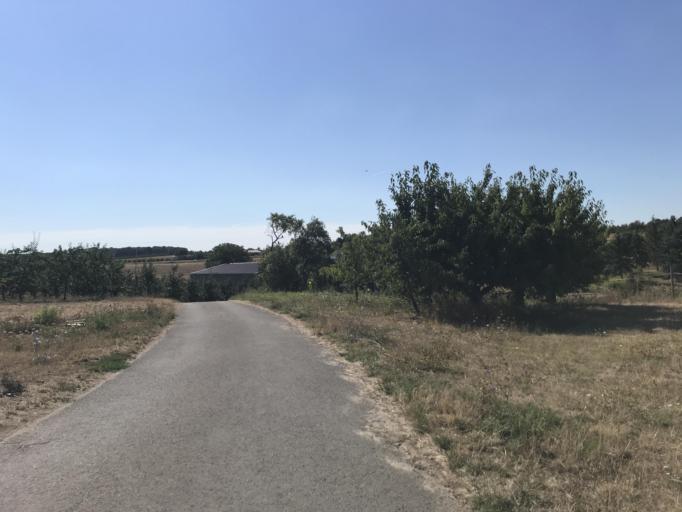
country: DE
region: Rheinland-Pfalz
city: Wackernheim
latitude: 49.9803
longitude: 8.1271
